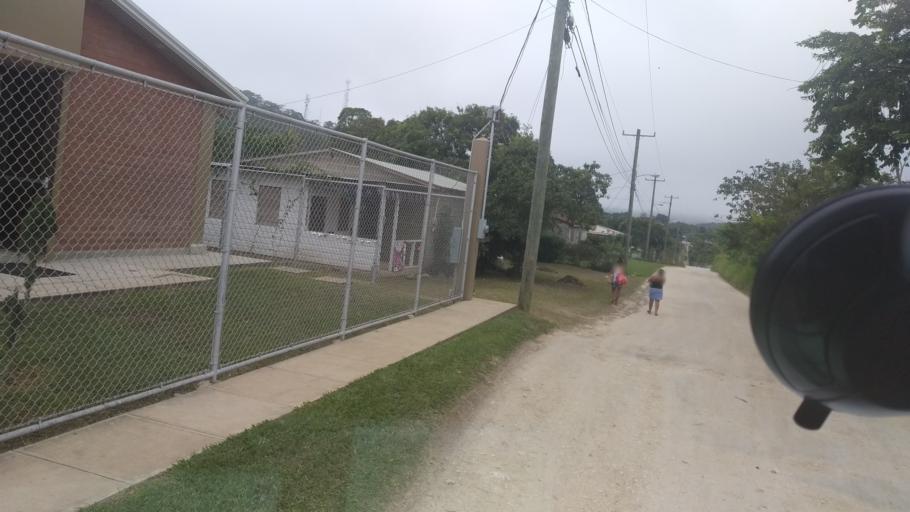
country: BZ
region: Cayo
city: Benque Viejo del Carmen
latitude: 17.0833
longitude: -89.1255
